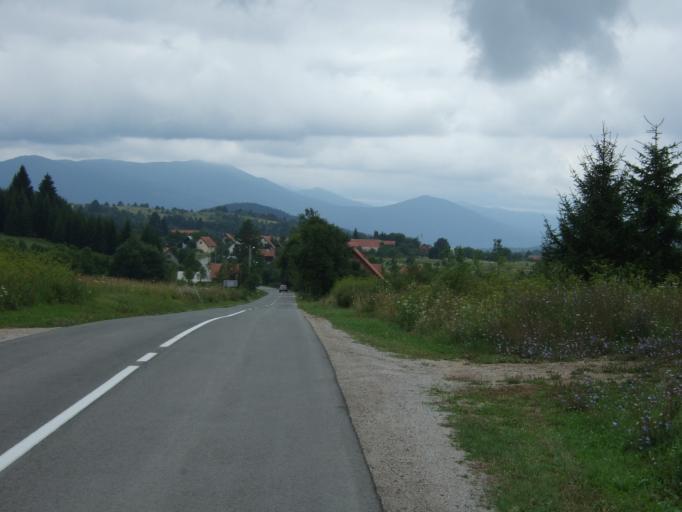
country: HR
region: Licko-Senjska
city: Jezerce
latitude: 44.9691
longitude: 15.5112
